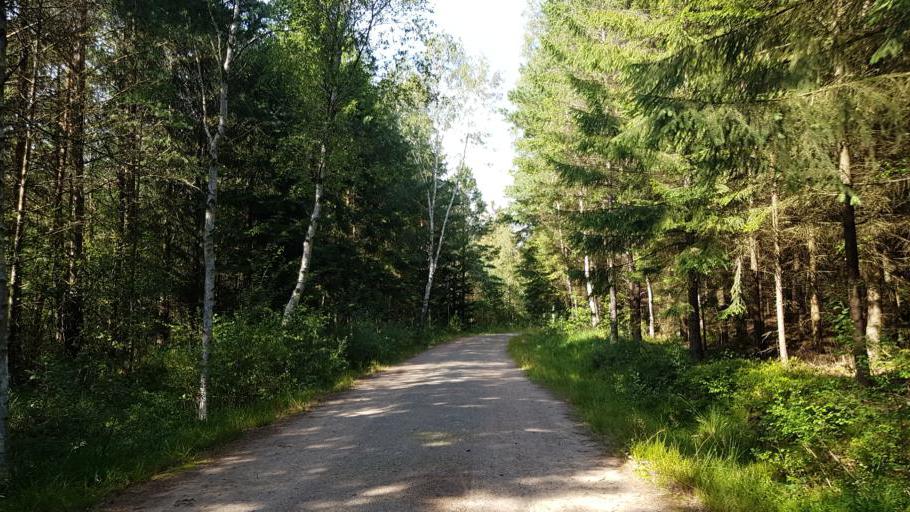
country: SE
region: Vaestra Goetaland
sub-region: Partille Kommun
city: Ojersjo
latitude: 57.6787
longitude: 12.0695
